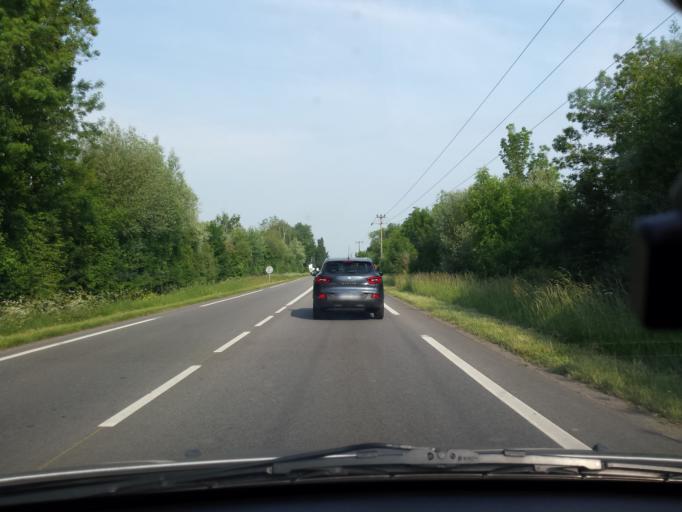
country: FR
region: Pays de la Loire
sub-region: Departement de la Loire-Atlantique
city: Machecoul
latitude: 46.9971
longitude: -1.8115
